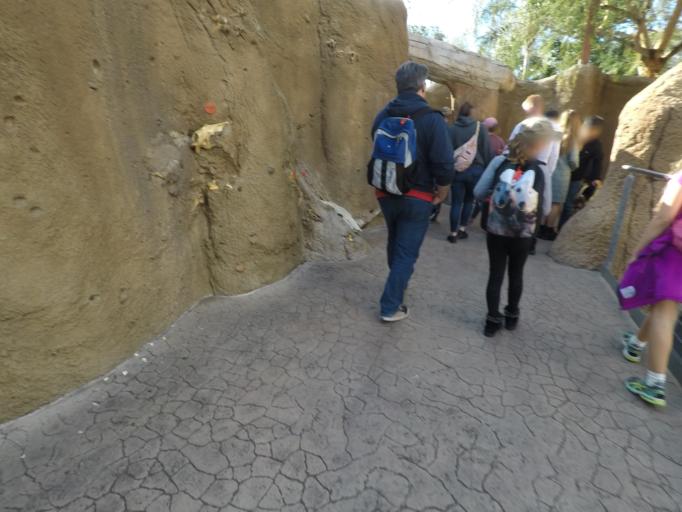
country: US
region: California
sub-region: San Diego County
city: San Diego
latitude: 32.7356
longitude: -117.1530
